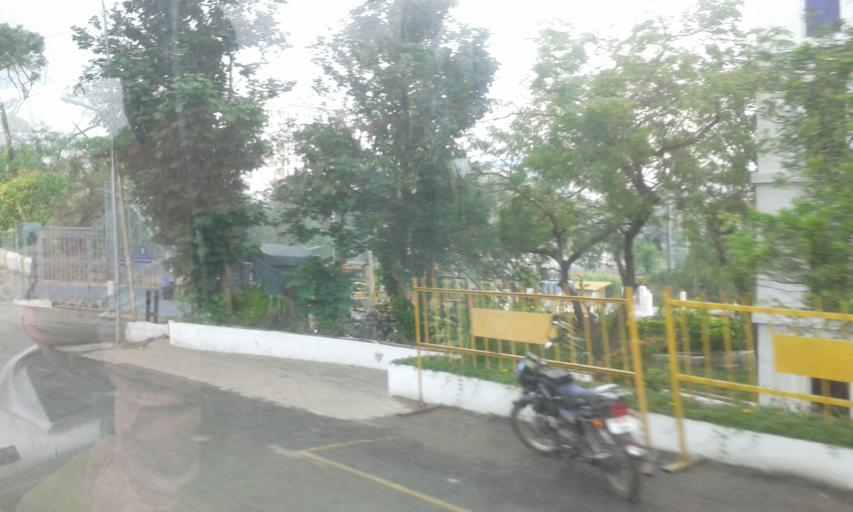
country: IN
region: Tamil Nadu
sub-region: Kancheepuram
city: Guduvancheri
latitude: 12.8241
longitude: 80.0412
